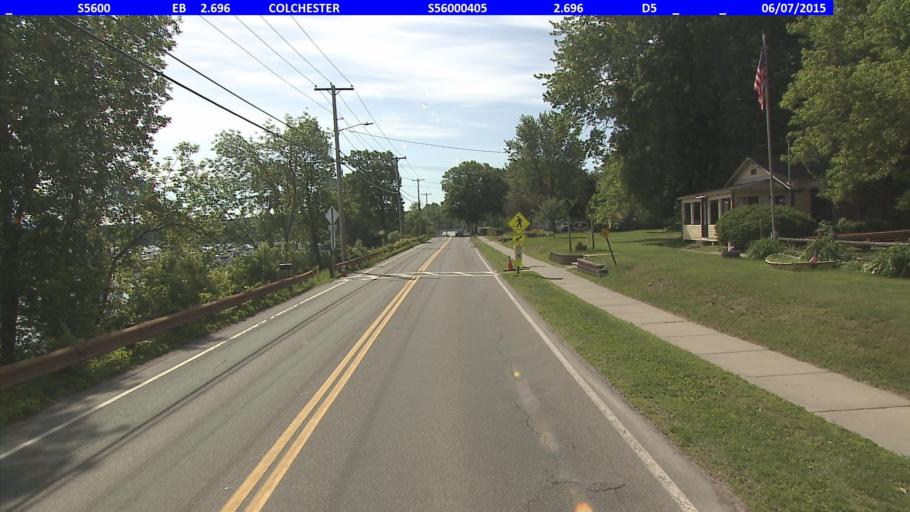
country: US
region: Vermont
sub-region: Chittenden County
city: Winooski
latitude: 44.5491
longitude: -73.2240
